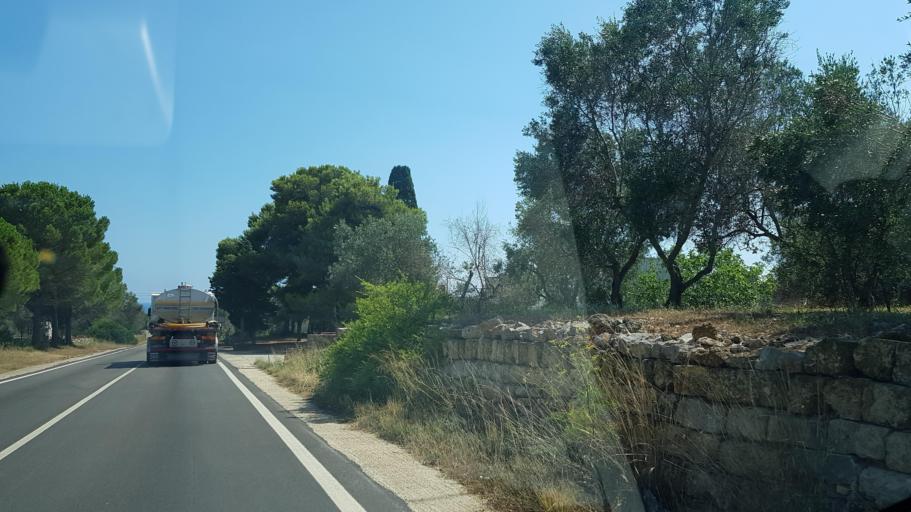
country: IT
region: Apulia
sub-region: Provincia di Lecce
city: Leuca
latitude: 39.8058
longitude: 18.3529
